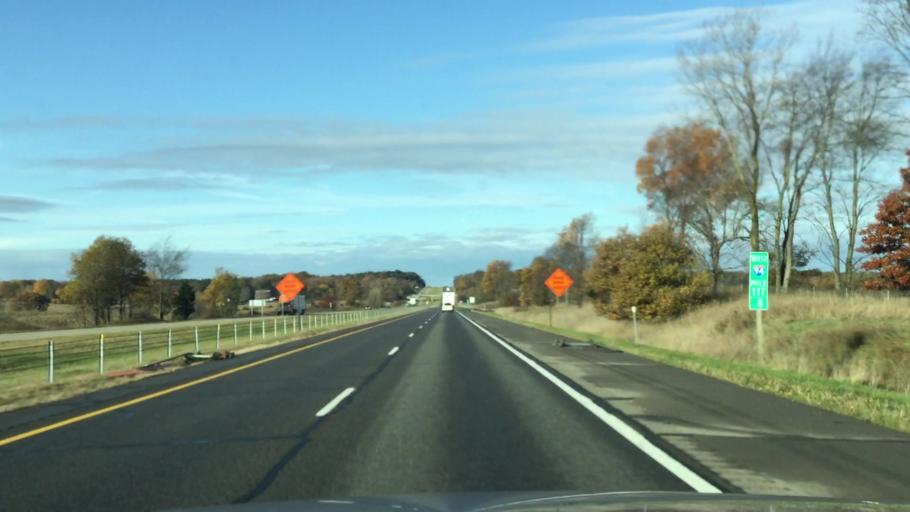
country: US
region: Michigan
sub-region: Calhoun County
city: Albion
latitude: 42.2839
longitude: -84.8160
